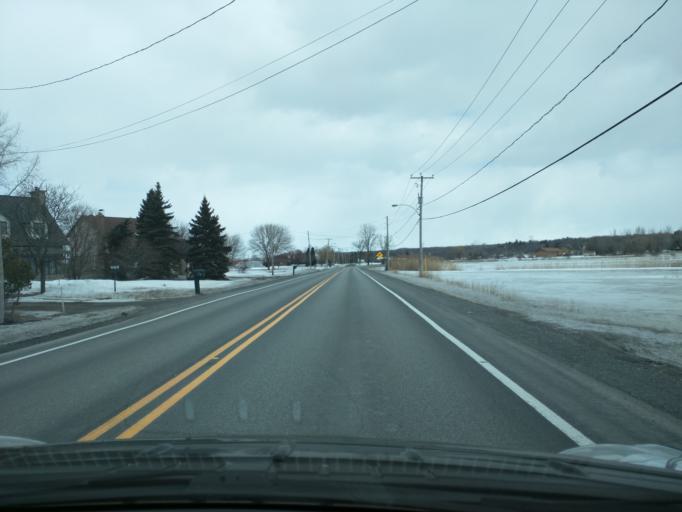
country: CA
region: Quebec
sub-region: Monteregie
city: Sainte-Julie
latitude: 45.6173
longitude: -73.3645
